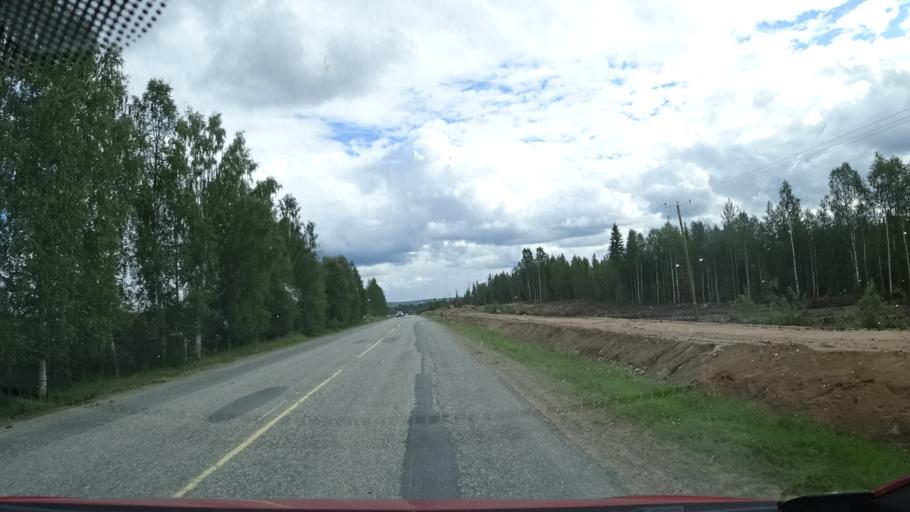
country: FI
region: Lapland
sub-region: Rovaniemi
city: Rovaniemi
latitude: 66.5429
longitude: 25.7126
